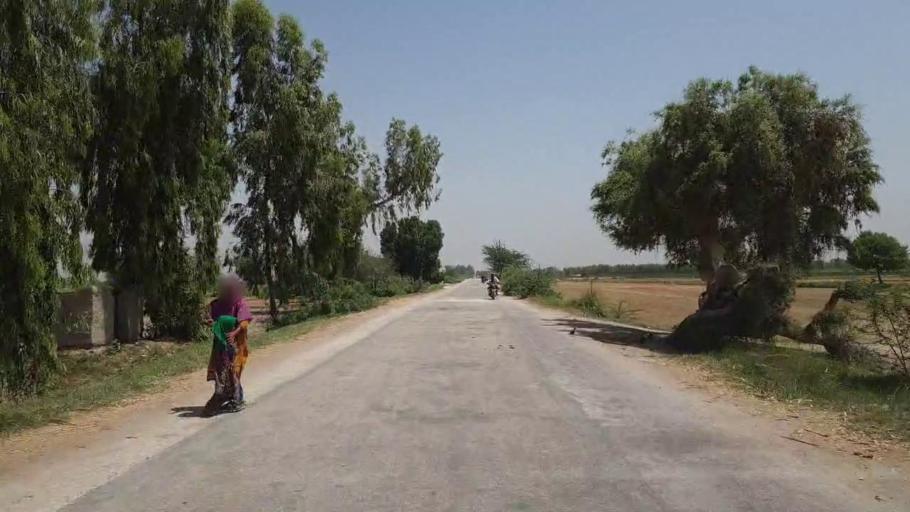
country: PK
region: Sindh
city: Adilpur
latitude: 27.9032
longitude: 69.2949
